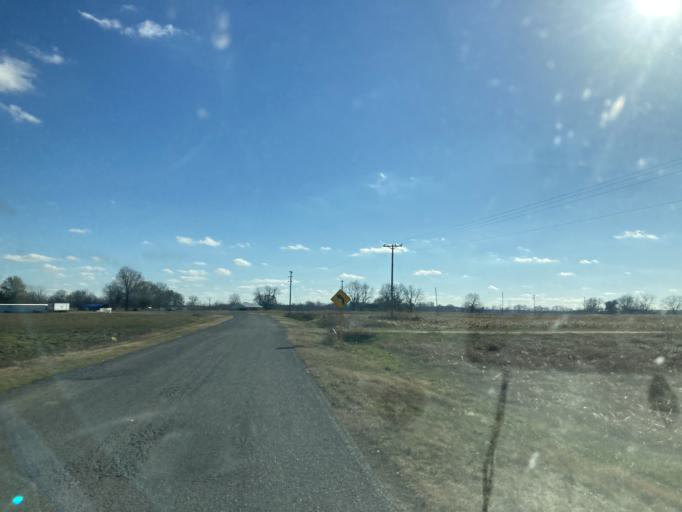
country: US
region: Mississippi
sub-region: Yazoo County
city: Yazoo City
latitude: 32.9293
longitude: -90.4717
